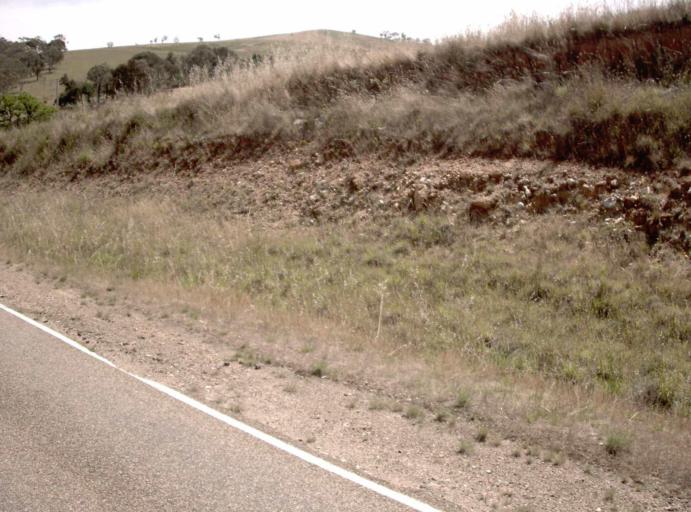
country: AU
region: Victoria
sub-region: Alpine
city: Mount Beauty
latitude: -37.0675
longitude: 147.6030
